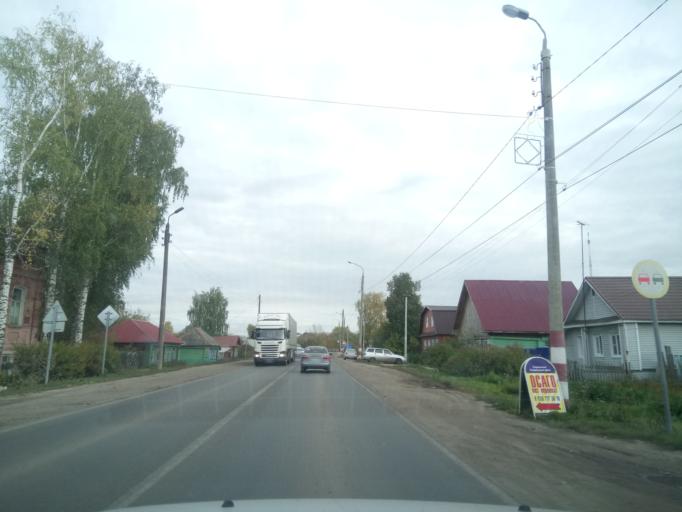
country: RU
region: Nizjnij Novgorod
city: Lukoyanov
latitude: 55.0303
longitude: 44.4874
